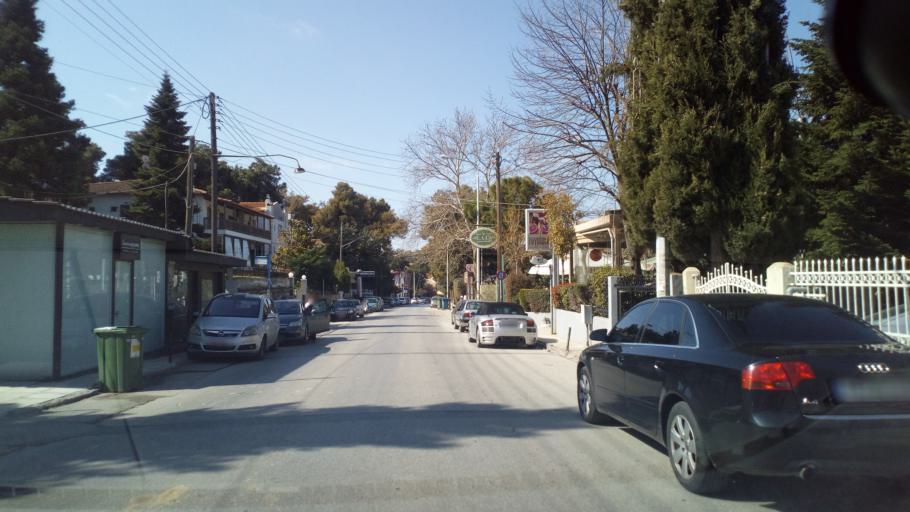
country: GR
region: Central Macedonia
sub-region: Nomos Thessalonikis
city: Panorama
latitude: 40.5925
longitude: 23.0414
